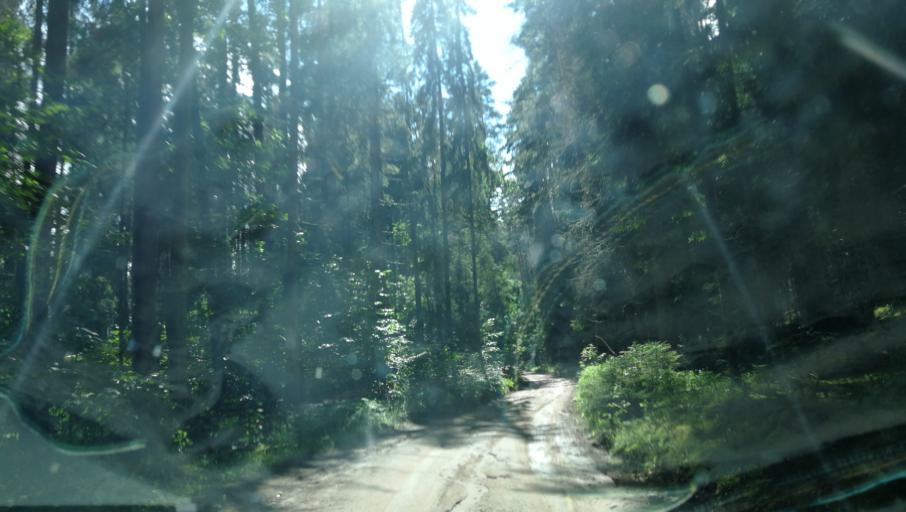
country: LV
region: Cesu Rajons
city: Cesis
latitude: 57.3091
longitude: 25.2153
